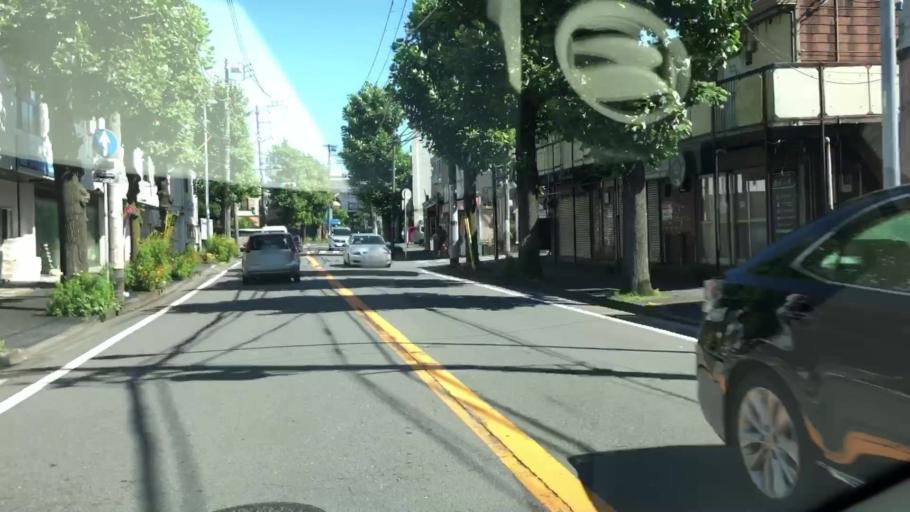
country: JP
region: Kanagawa
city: Yokohama
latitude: 35.3839
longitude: 139.6038
